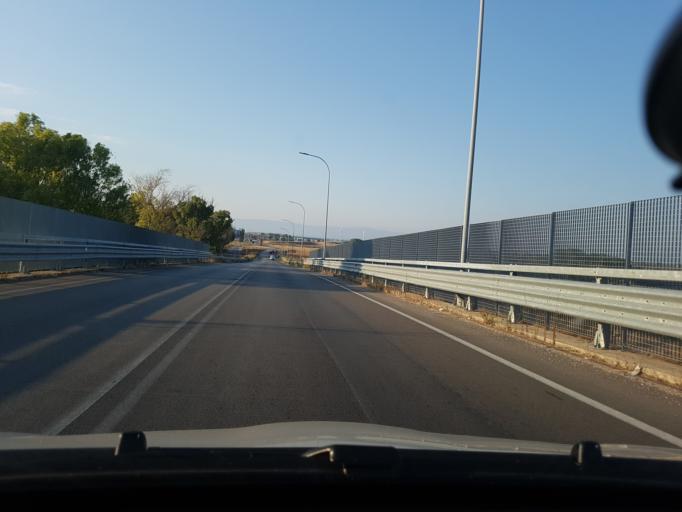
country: IT
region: Apulia
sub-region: Provincia di Foggia
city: Carapelle
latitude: 41.4072
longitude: 15.6532
